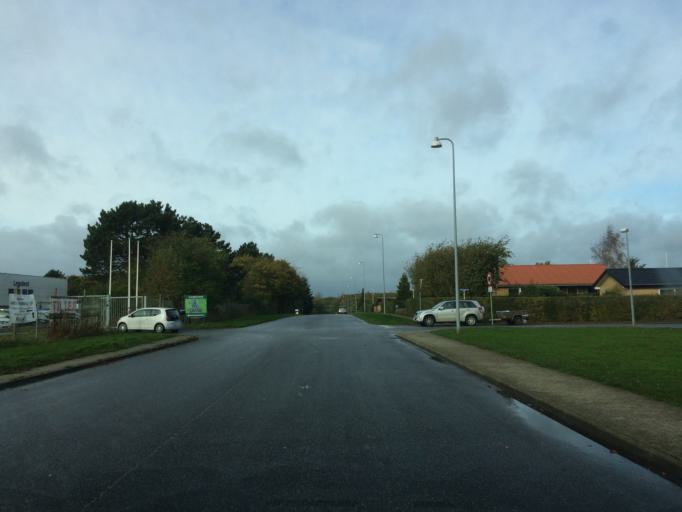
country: DK
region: South Denmark
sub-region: Fredericia Kommune
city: Fredericia
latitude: 55.5786
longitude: 9.7451
